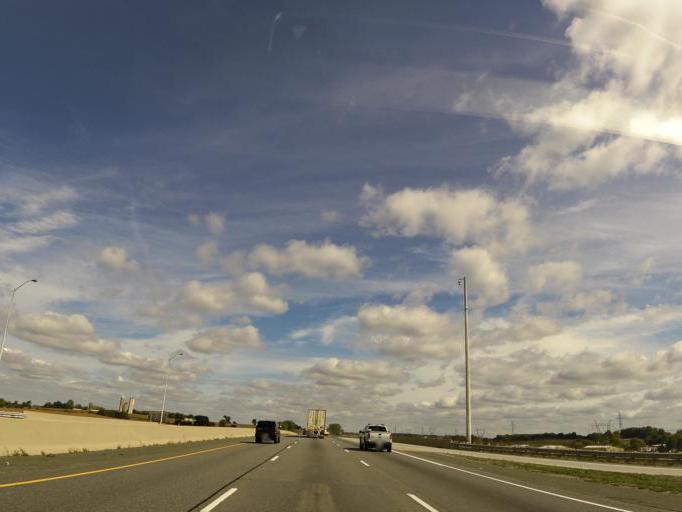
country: CA
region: Ontario
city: Ingersoll
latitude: 42.9756
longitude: -80.9515
